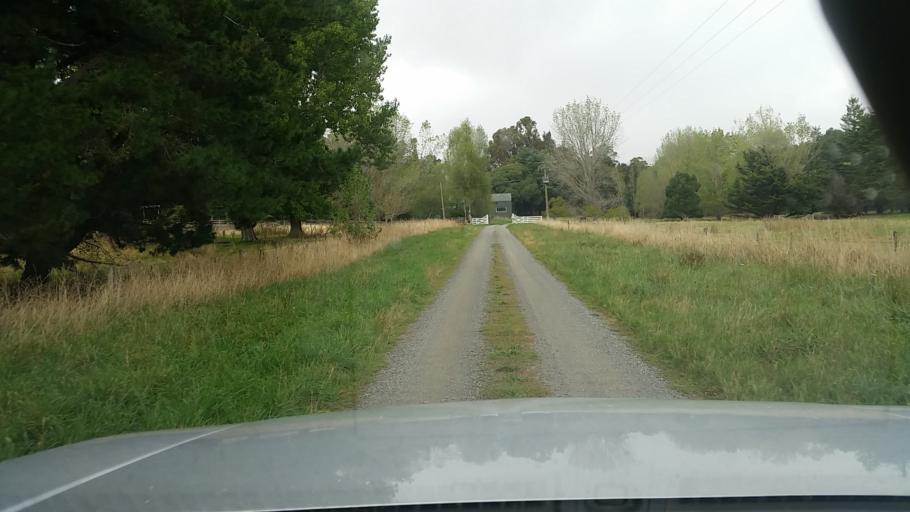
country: NZ
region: Marlborough
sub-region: Marlborough District
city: Blenheim
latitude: -41.7323
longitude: 173.9226
